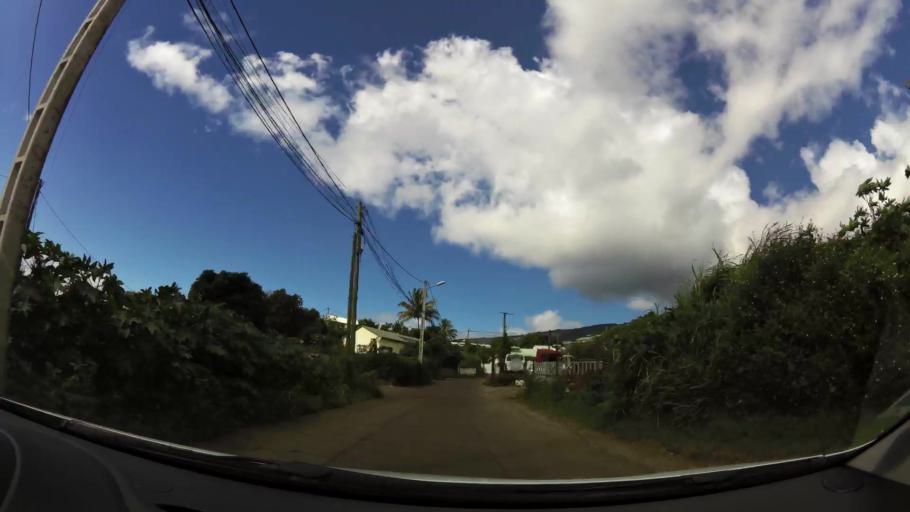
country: RE
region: Reunion
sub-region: Reunion
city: Sainte-Marie
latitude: -20.9238
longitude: 55.4994
